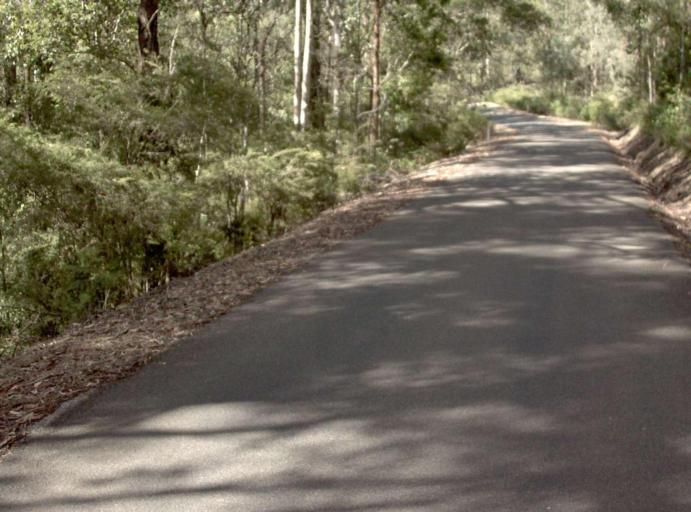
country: AU
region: Victoria
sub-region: East Gippsland
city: Lakes Entrance
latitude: -37.4593
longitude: 148.1222
